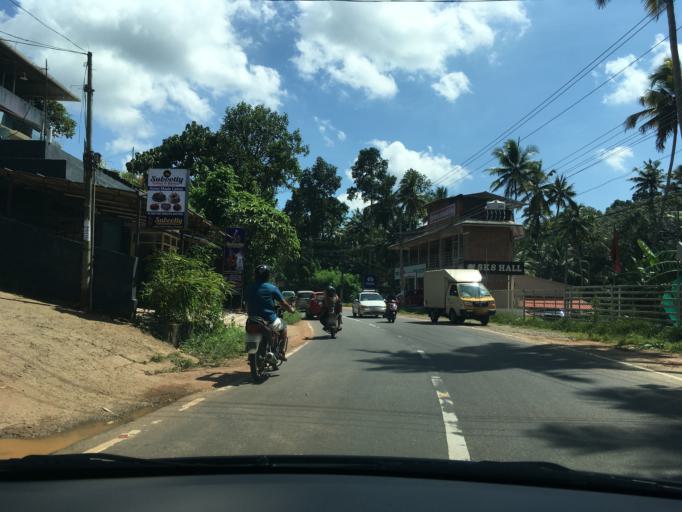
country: IN
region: Kerala
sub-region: Thiruvananthapuram
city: Nedumangad
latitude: 8.5867
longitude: 76.9957
